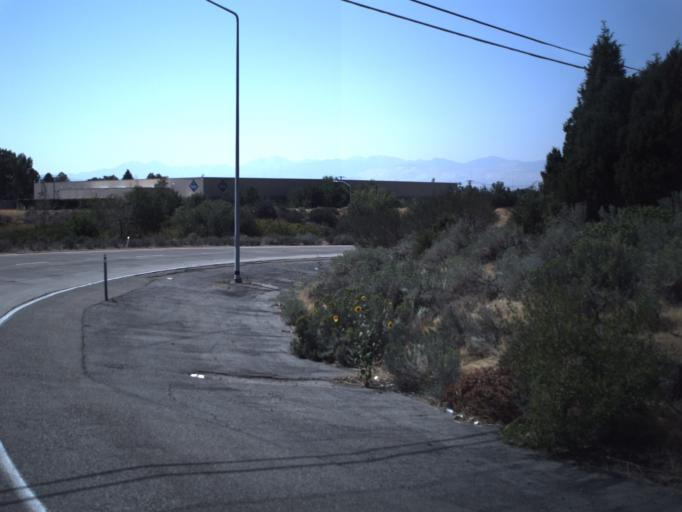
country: US
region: Utah
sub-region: Salt Lake County
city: Midvale
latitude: 40.6324
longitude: -111.8835
